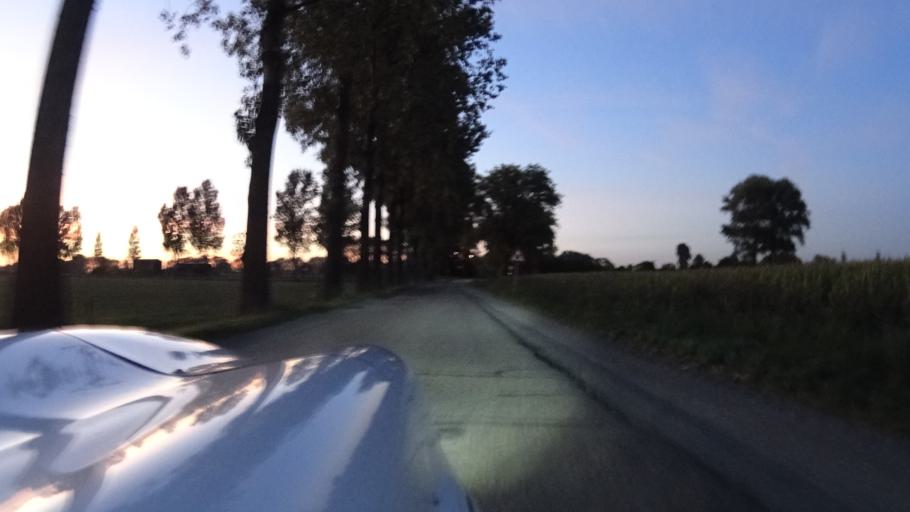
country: NL
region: North Brabant
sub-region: Gemeente Aalburg
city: Aalburg
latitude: 51.7617
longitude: 5.0760
